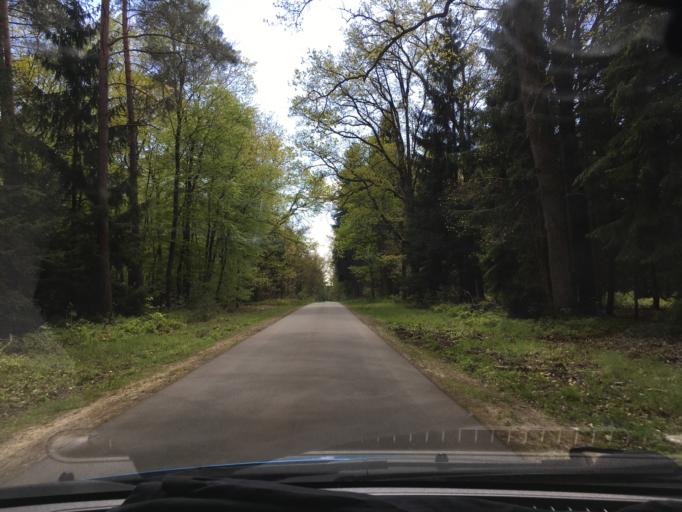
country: DE
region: Lower Saxony
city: Boitze
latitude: 53.1180
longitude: 10.7906
